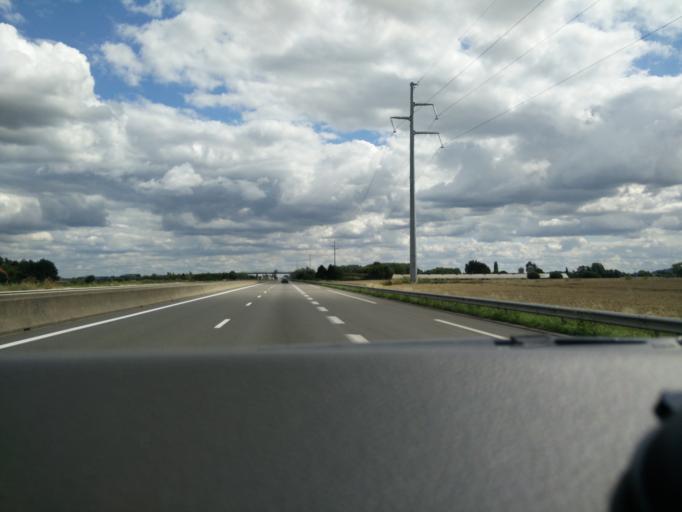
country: FR
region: Nord-Pas-de-Calais
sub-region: Departement du Nord
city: Herzeele
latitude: 50.8822
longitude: 2.5182
